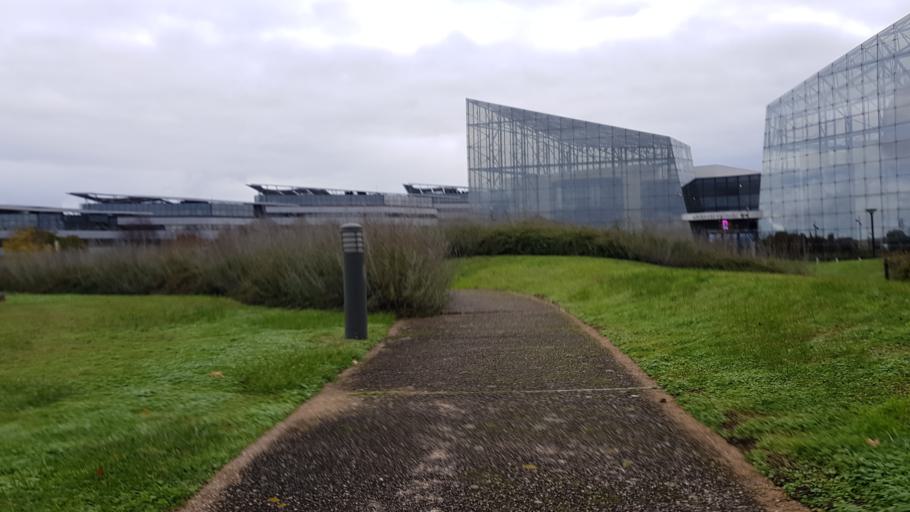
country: FR
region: Poitou-Charentes
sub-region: Departement de la Vienne
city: Chasseneuil-du-Poitou
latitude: 46.6615
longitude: 0.3642
